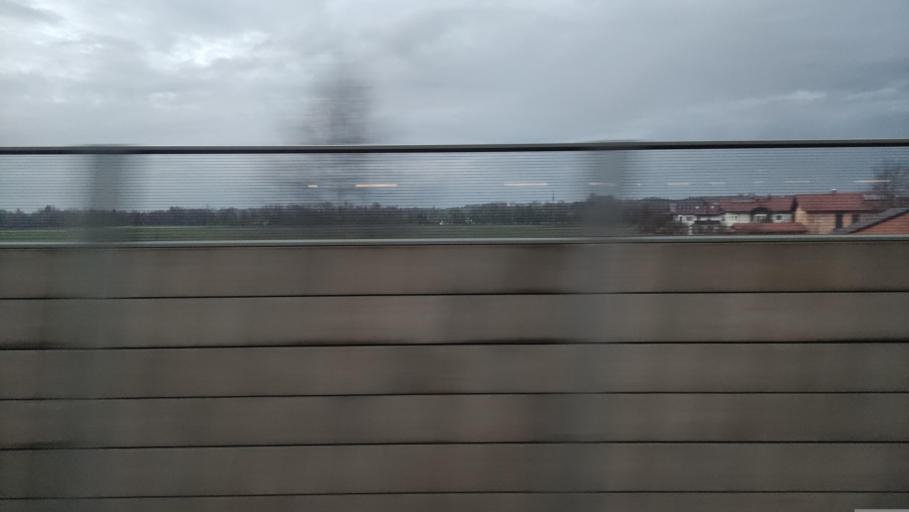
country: DE
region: Bavaria
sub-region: Upper Bavaria
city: Ampfing
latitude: 48.2538
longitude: 12.4008
